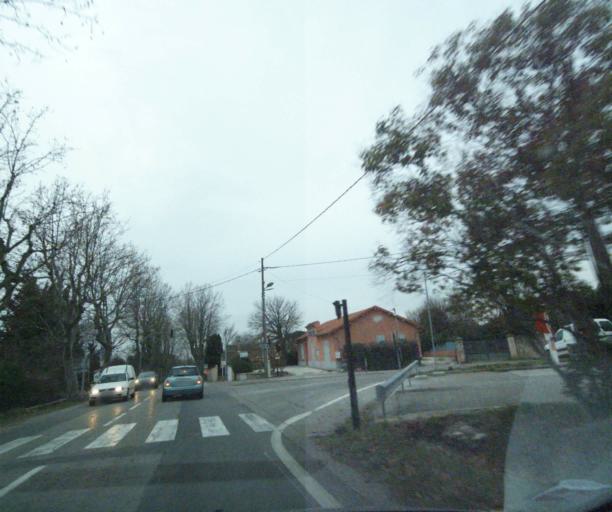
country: FR
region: Provence-Alpes-Cote d'Azur
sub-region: Departement des Bouches-du-Rhone
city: Aix-en-Provence
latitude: 43.5597
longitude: 5.4616
